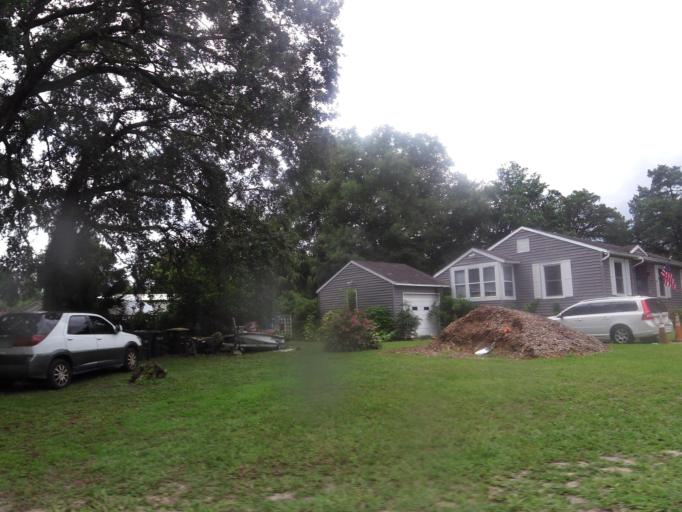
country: US
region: Florida
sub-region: Duval County
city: Jacksonville
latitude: 30.2980
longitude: -81.5560
